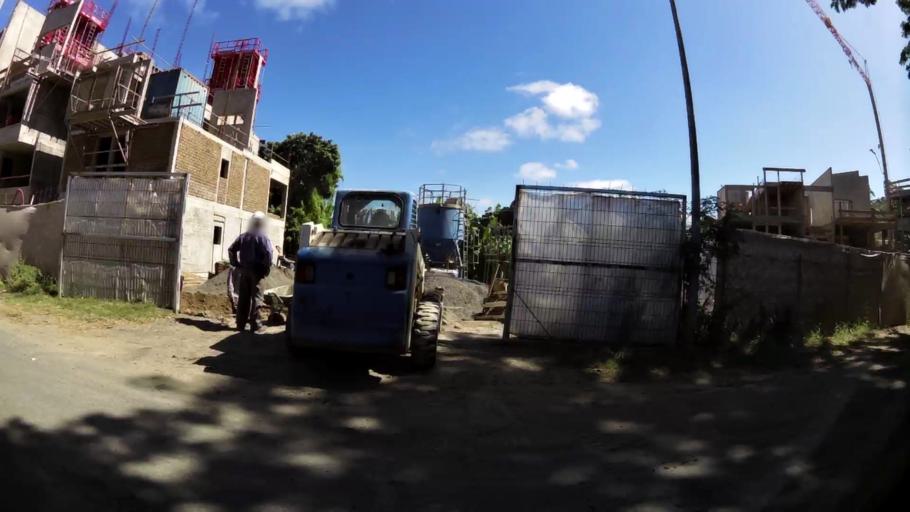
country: YT
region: Pamandzi
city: Pamandzi
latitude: -12.7959
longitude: 45.2793
